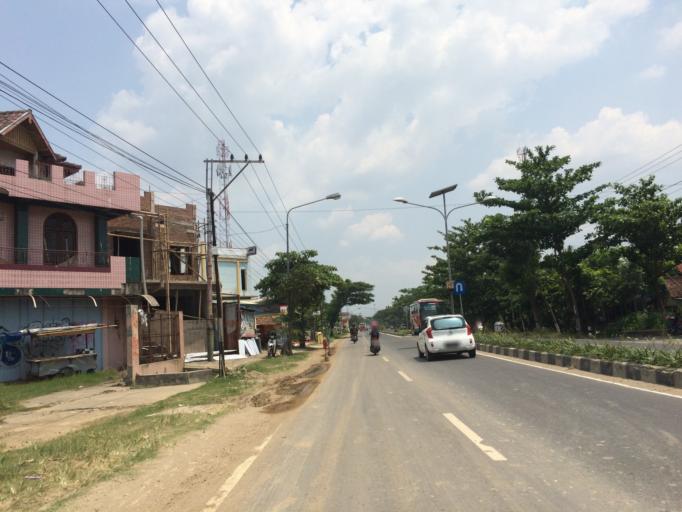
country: ID
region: Central Java
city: Grogol
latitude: -7.6413
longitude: 110.8294
